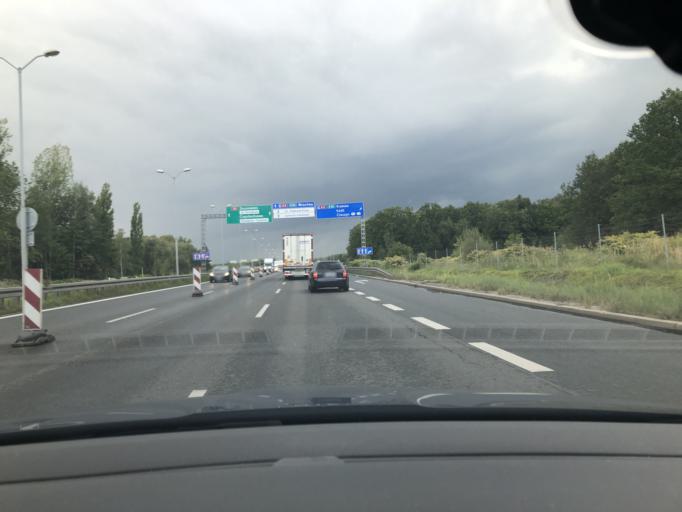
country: PL
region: Silesian Voivodeship
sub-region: Katowice
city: Katowice
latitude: 50.2362
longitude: 19.0543
